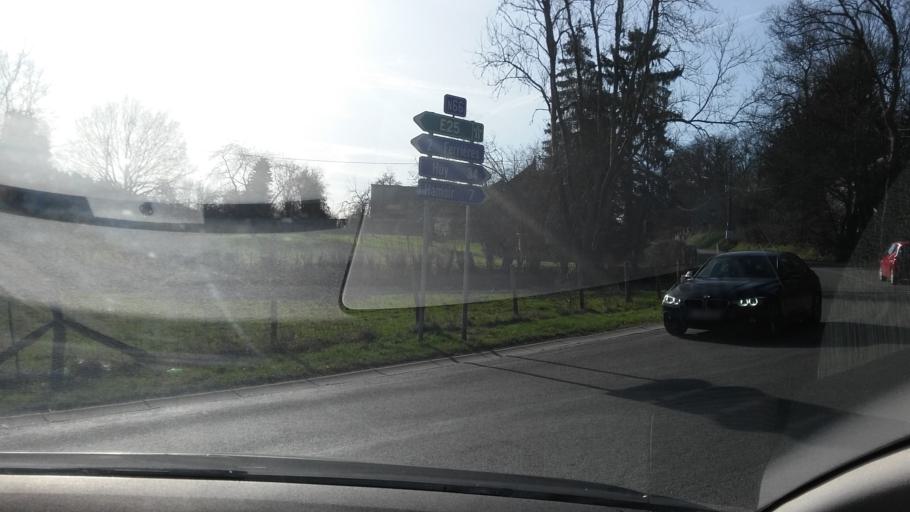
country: BE
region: Wallonia
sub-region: Province de Liege
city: Ferrieres
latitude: 50.4106
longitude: 5.6029
